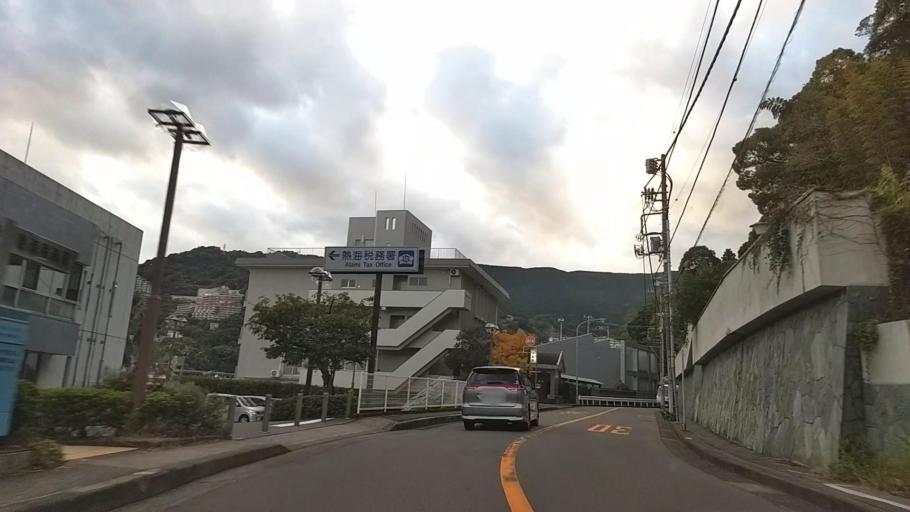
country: JP
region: Shizuoka
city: Atami
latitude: 35.0989
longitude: 139.0719
